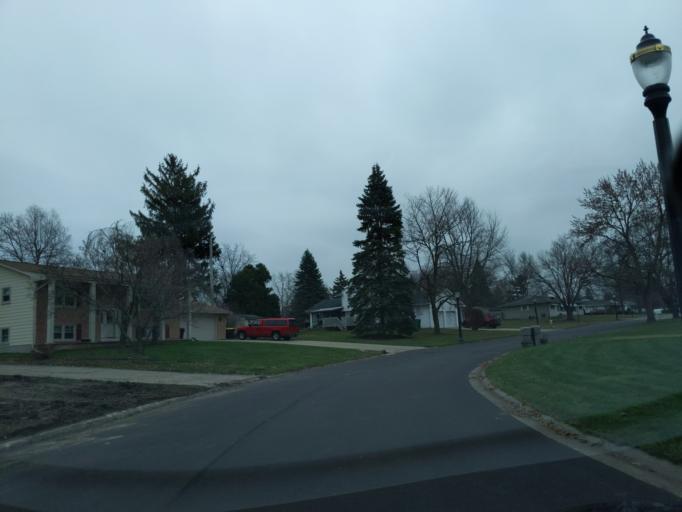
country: US
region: Michigan
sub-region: Eaton County
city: Waverly
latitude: 42.7285
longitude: -84.6296
